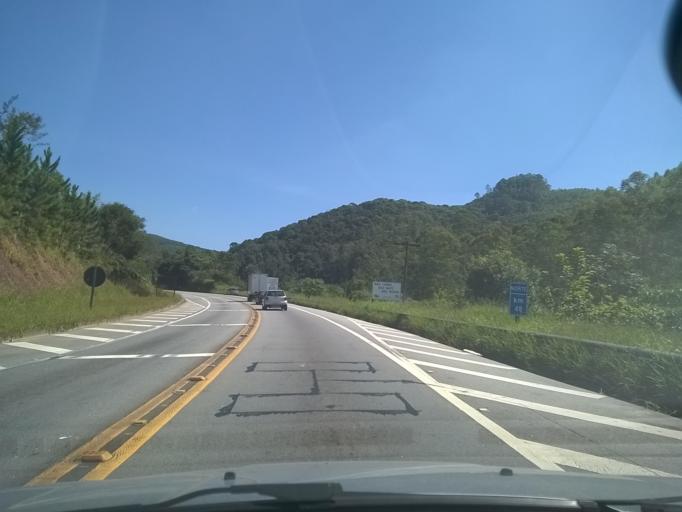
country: BR
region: Sao Paulo
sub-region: Francisco Morato
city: Francisco Morato
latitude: -23.2837
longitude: -46.8003
